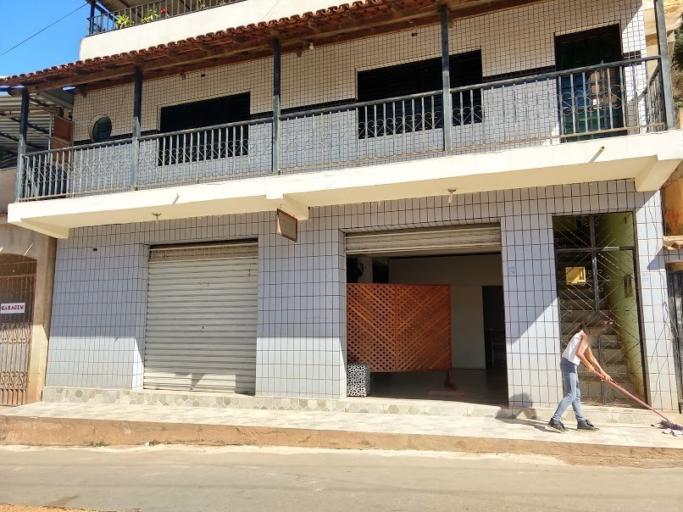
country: BR
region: Minas Gerais
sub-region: Vicosa
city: Vicosa
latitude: -20.6880
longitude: -42.6176
